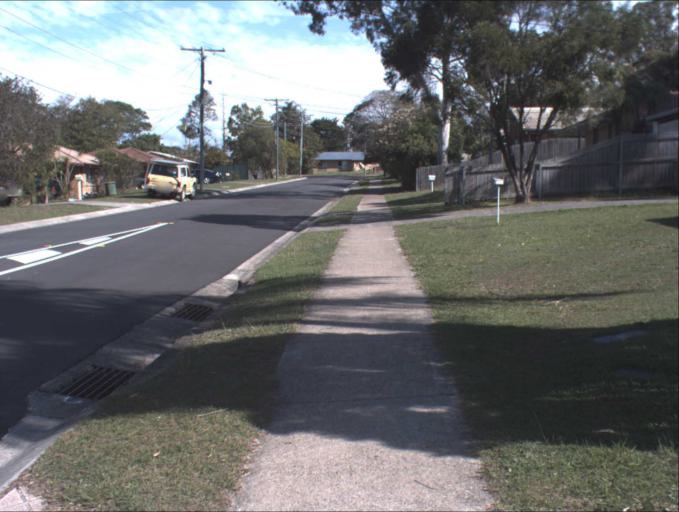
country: AU
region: Queensland
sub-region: Logan
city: Woodridge
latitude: -27.6651
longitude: 153.0567
